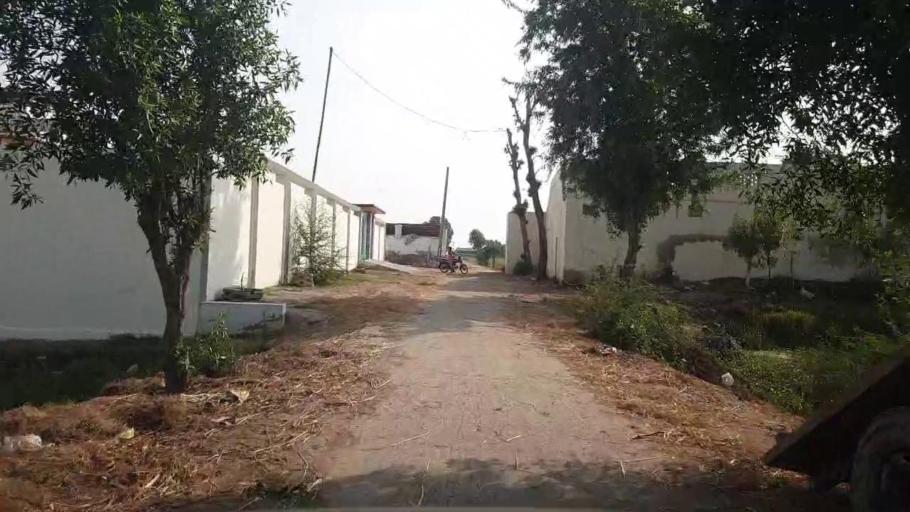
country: PK
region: Sindh
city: Kario
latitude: 24.6379
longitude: 68.5580
